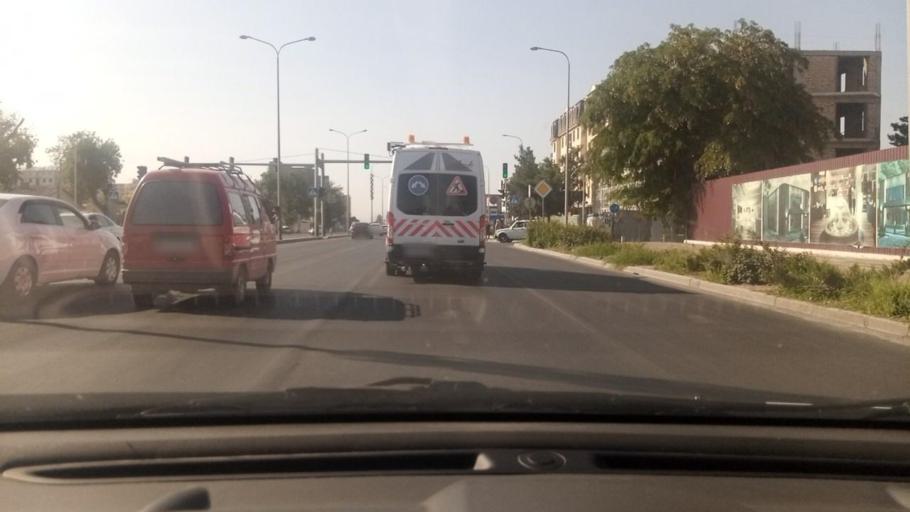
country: UZ
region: Toshkent Shahri
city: Bektemir
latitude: 41.2447
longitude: 69.3267
